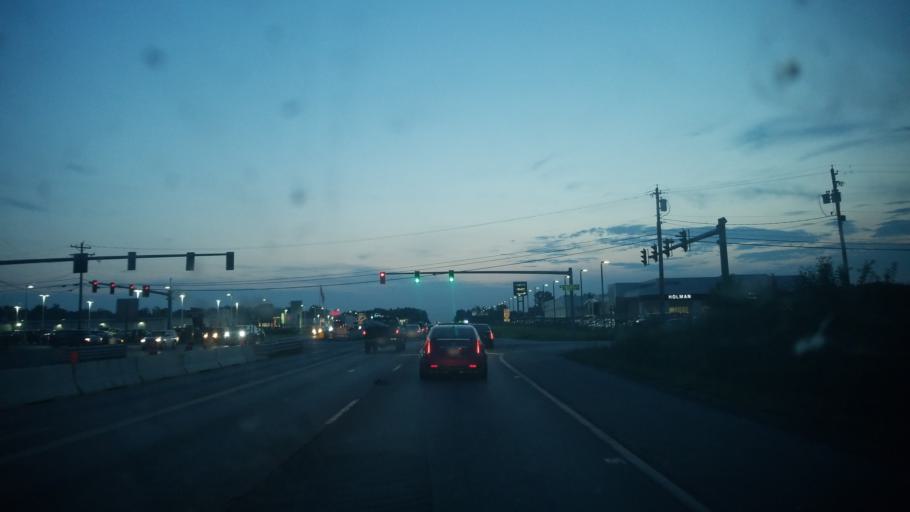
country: US
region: Ohio
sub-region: Clermont County
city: Summerside
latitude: 39.0907
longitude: -84.2474
